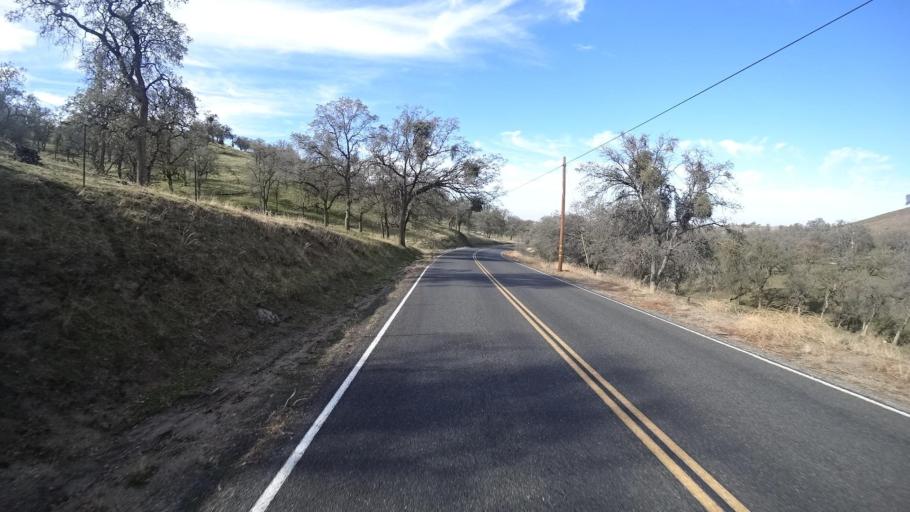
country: US
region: California
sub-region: Kern County
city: Alta Sierra
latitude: 35.6285
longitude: -118.8130
